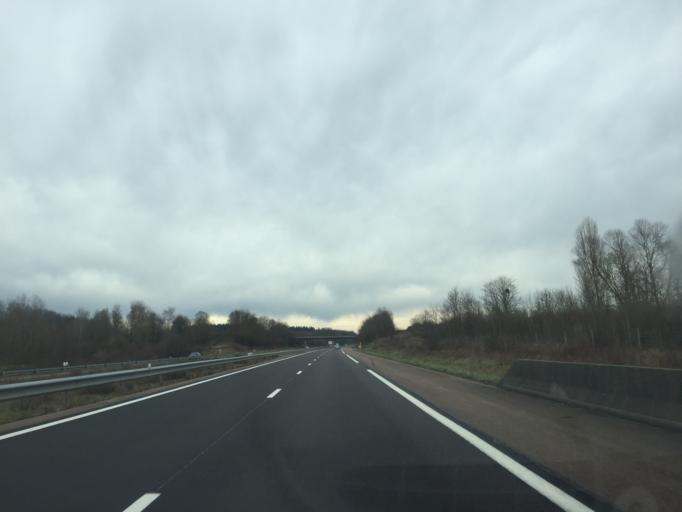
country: FR
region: Franche-Comte
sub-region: Departement du Jura
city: Bletterans
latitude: 46.8267
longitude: 5.5446
